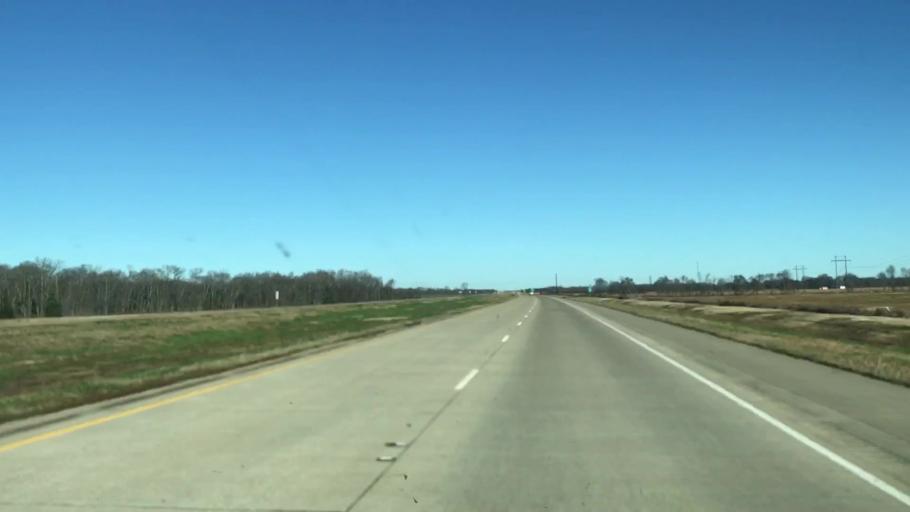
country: US
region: Louisiana
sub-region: Caddo Parish
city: Blanchard
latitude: 32.6559
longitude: -93.8423
